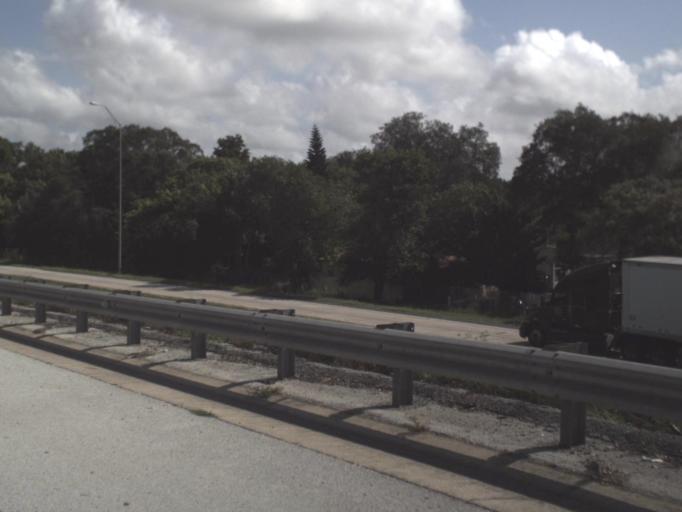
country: US
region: Florida
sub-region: Hillsborough County
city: University
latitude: 28.0558
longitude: -82.4546
